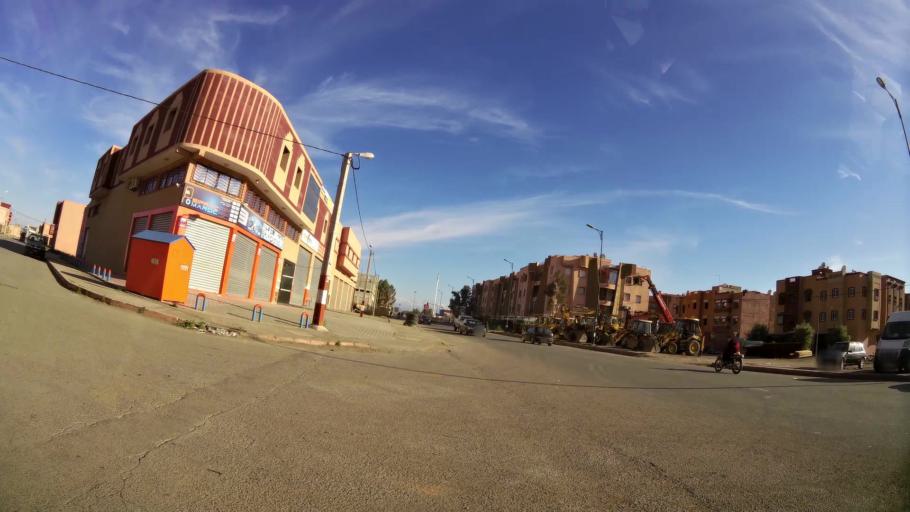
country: MA
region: Marrakech-Tensift-Al Haouz
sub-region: Marrakech
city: Marrakesh
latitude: 31.6844
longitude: -8.0616
